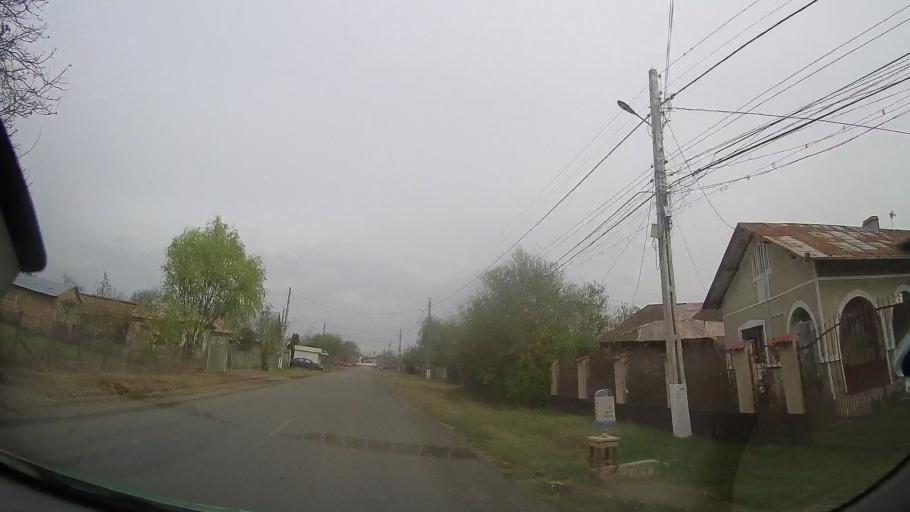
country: RO
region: Prahova
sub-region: Comuna Balta Doamnei
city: Balta Doamnei
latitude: 44.7590
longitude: 26.1646
